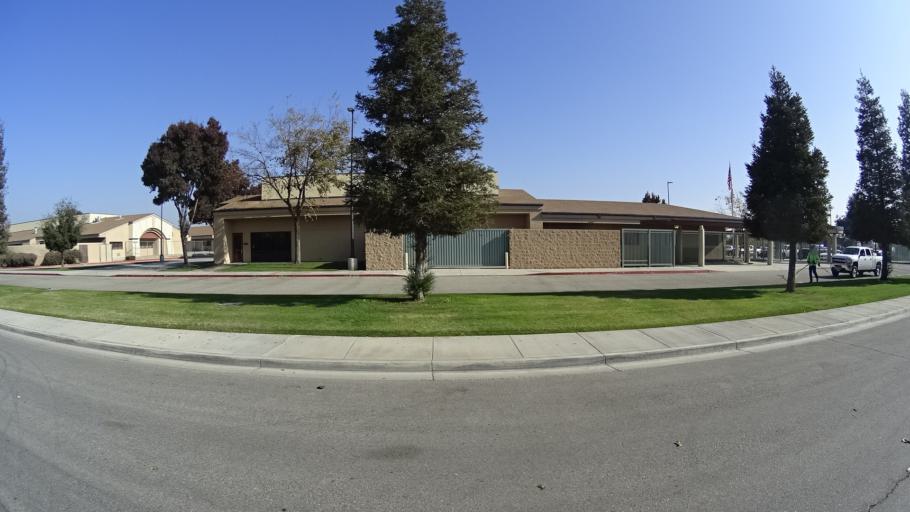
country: US
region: California
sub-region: Kern County
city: Greenfield
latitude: 35.2783
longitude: -119.0119
